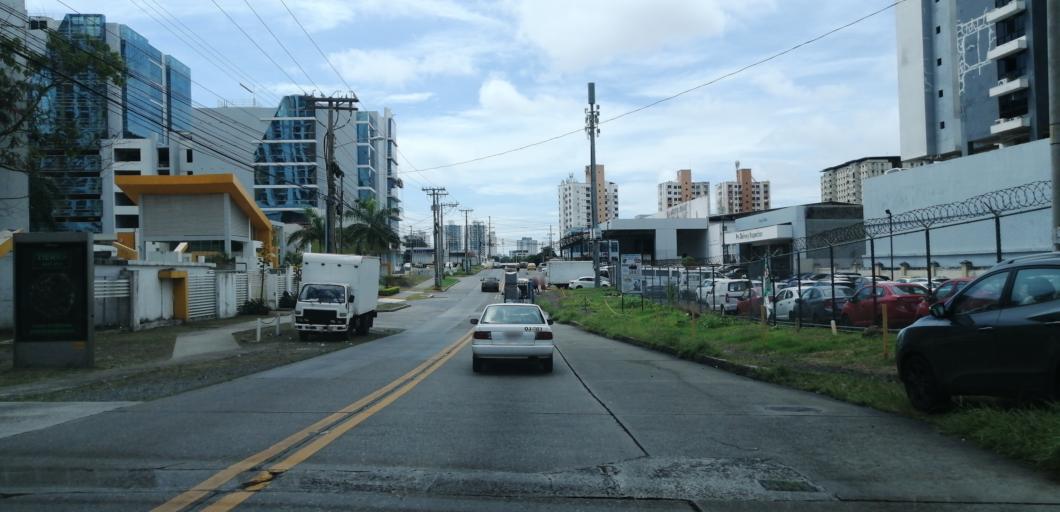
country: PA
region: Panama
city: Panama
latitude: 9.0266
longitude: -79.5240
